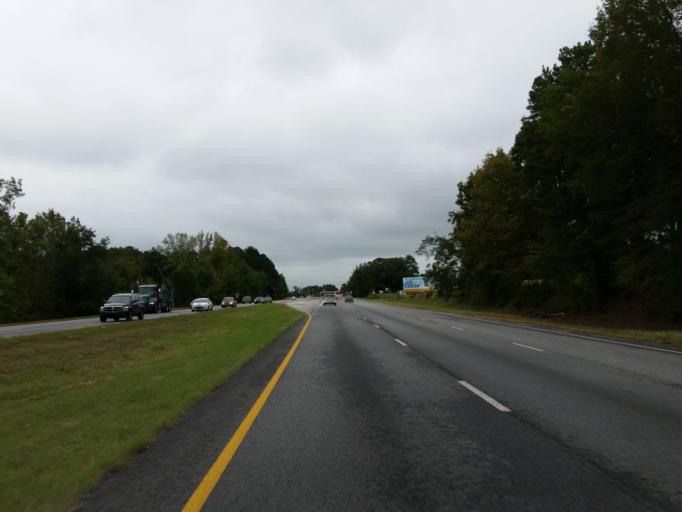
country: US
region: Georgia
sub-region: Henry County
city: Hampton
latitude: 33.3560
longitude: -84.2963
